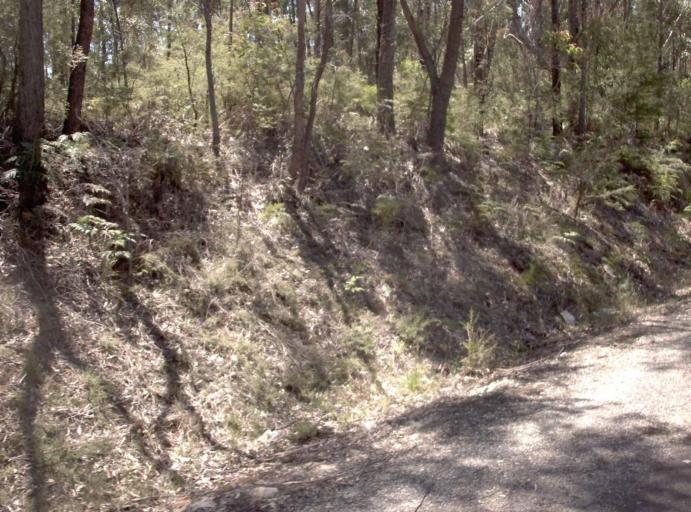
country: AU
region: Victoria
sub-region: East Gippsland
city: Lakes Entrance
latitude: -37.6935
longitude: 148.6139
